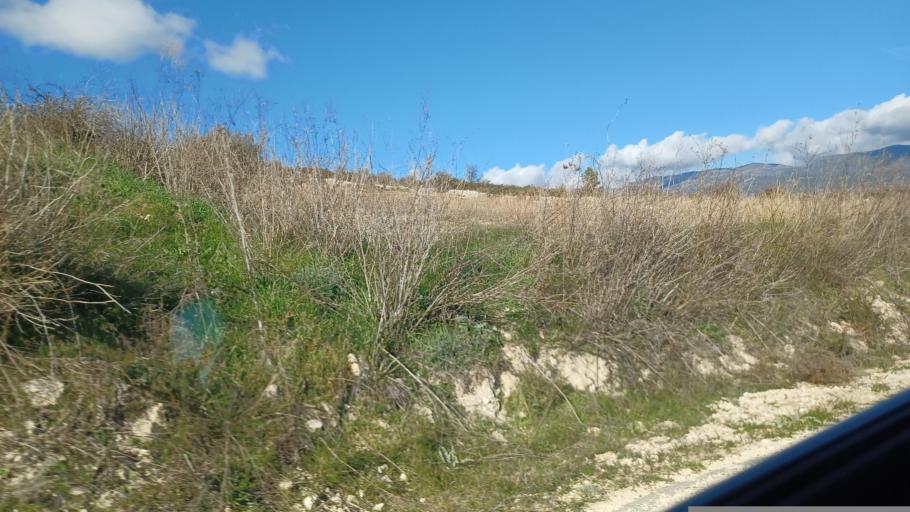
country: CY
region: Limassol
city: Pachna
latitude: 34.8388
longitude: 32.8045
